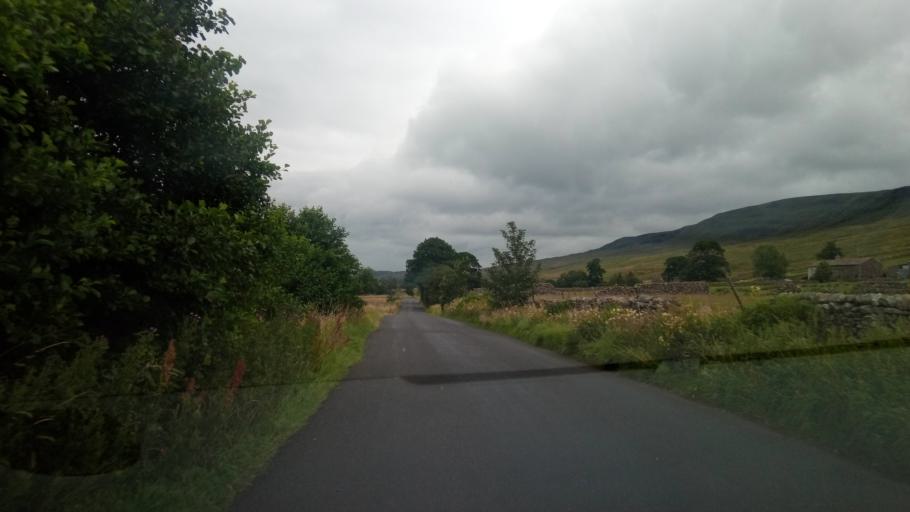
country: GB
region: England
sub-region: Cumbria
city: Kirkby Stephen
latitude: 54.3889
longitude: -2.3372
